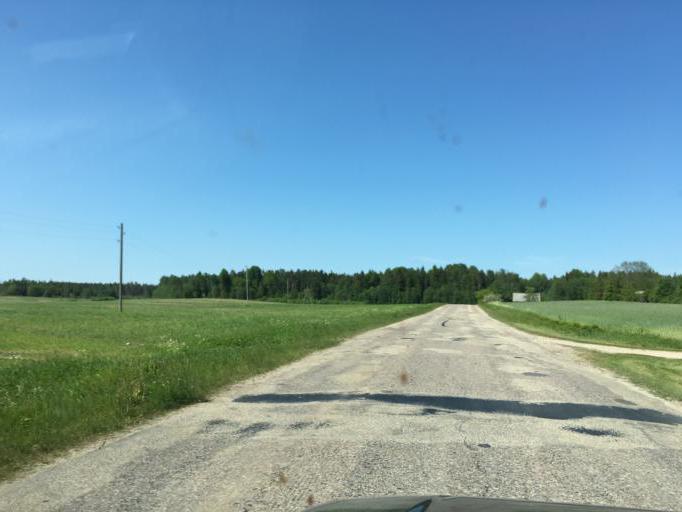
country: LV
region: Dundaga
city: Dundaga
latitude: 57.4717
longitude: 22.3220
